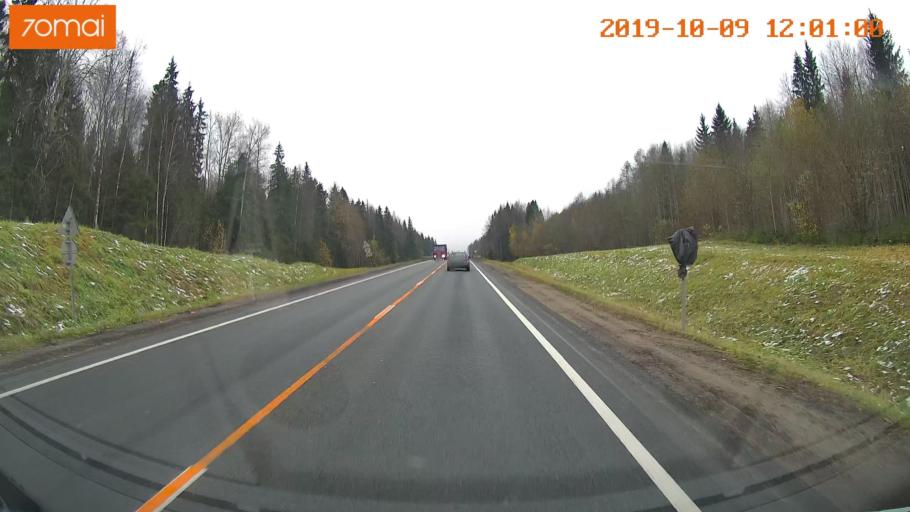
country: RU
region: Vologda
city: Gryazovets
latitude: 58.6928
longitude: 40.3014
